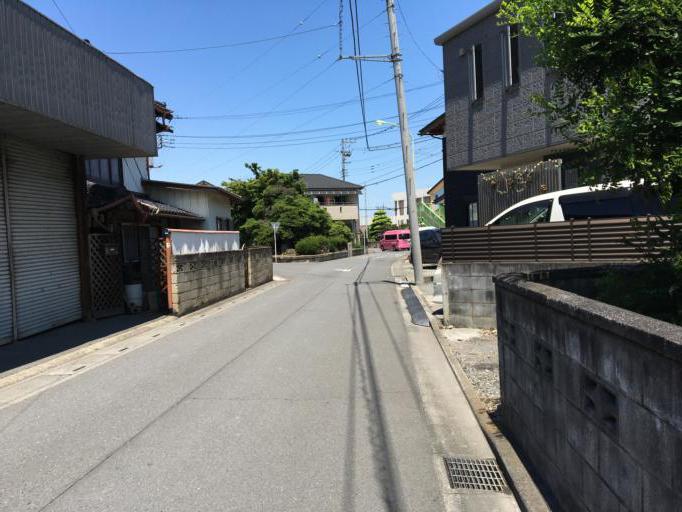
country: JP
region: Saitama
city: Sakado
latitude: 35.9380
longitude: 139.3881
